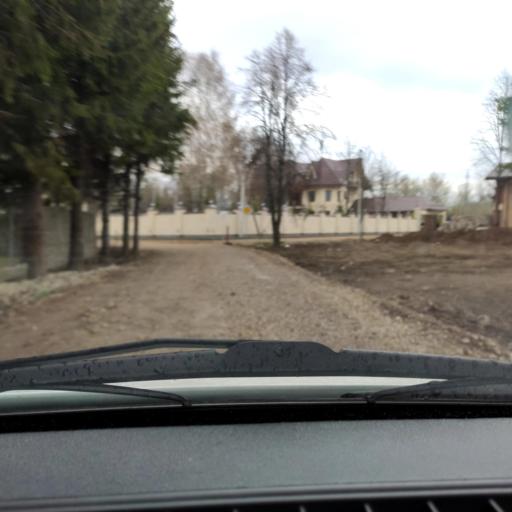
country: RU
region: Bashkortostan
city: Ufa
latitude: 54.7810
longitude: 56.1817
